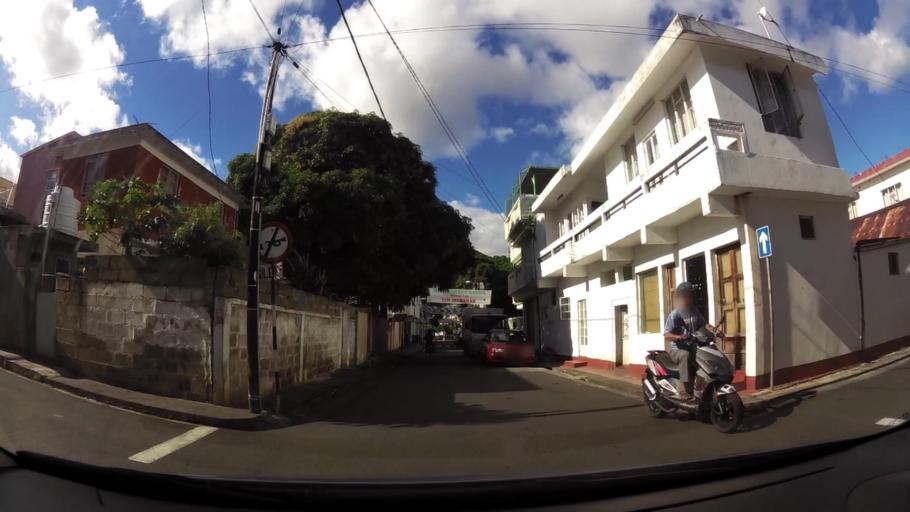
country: MU
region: Port Louis
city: Port Louis
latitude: -20.1546
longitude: 57.5161
